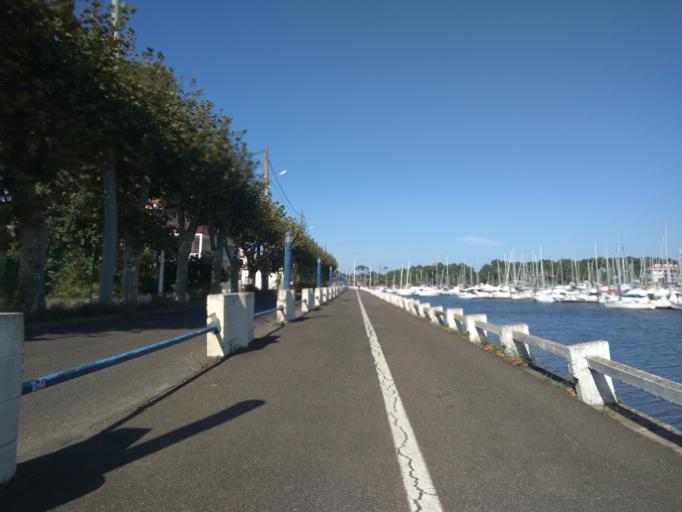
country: FR
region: Aquitaine
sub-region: Departement des Landes
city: Capbreton
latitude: 43.6507
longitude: -1.4363
